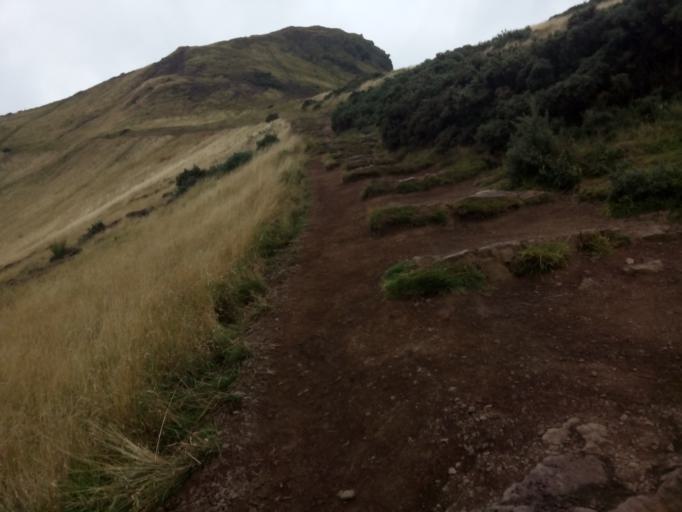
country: GB
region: Scotland
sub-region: West Lothian
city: Seafield
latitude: 55.9466
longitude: -3.1615
